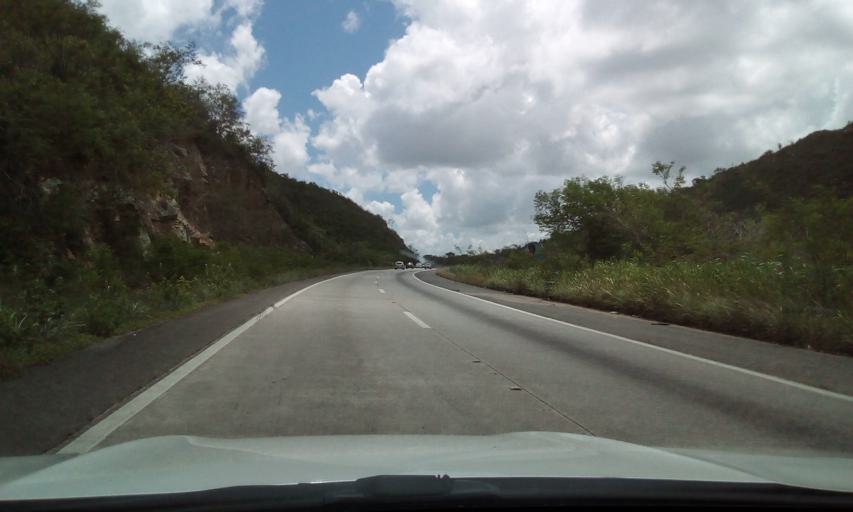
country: BR
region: Pernambuco
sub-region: Cha Grande
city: Cha Grande
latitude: -8.1676
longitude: -35.4695
